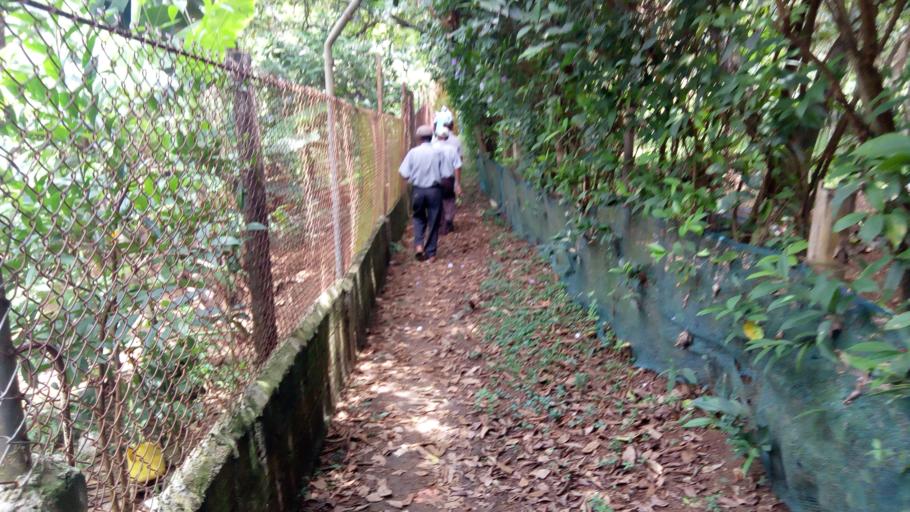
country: CO
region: Valle del Cauca
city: Cali
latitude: 3.3805
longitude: -76.5636
